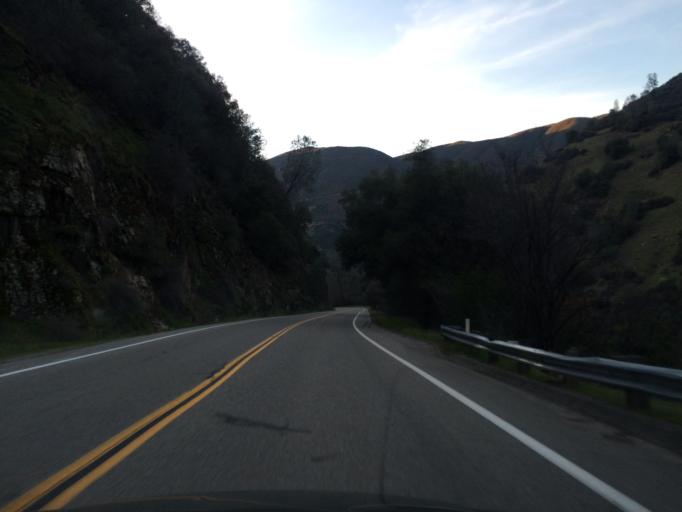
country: US
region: California
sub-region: Mariposa County
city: Midpines
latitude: 37.5995
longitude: -119.9592
